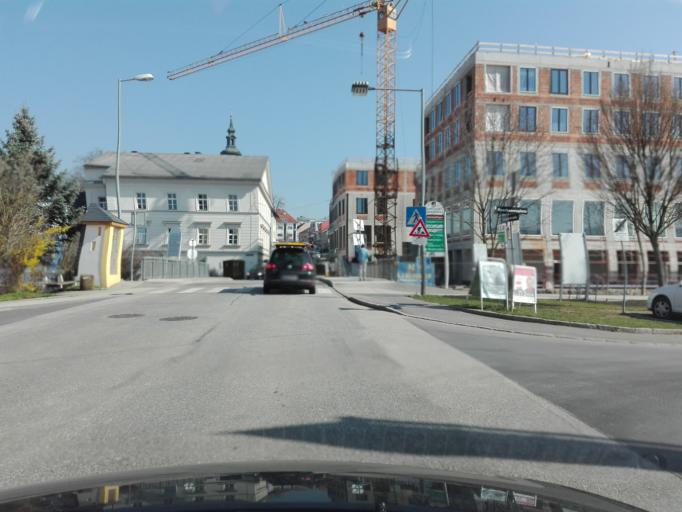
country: AT
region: Upper Austria
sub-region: Politischer Bezirk Urfahr-Umgebung
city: Gallneukirchen
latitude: 48.3517
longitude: 14.4140
